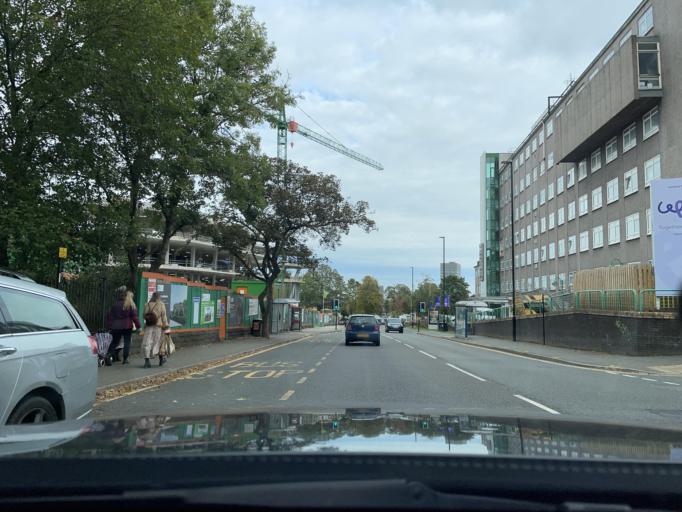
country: GB
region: England
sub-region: Sheffield
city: Sheffield
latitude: 53.3801
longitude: -1.4961
